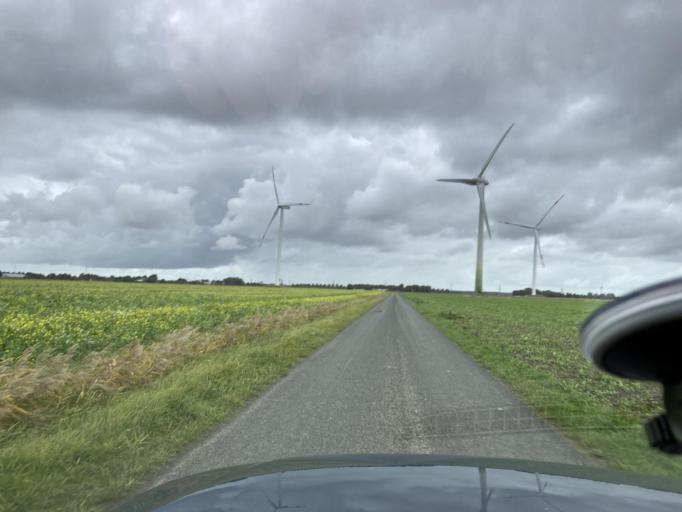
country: DE
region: Schleswig-Holstein
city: Norderwohrden
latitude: 54.2068
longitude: 9.0063
